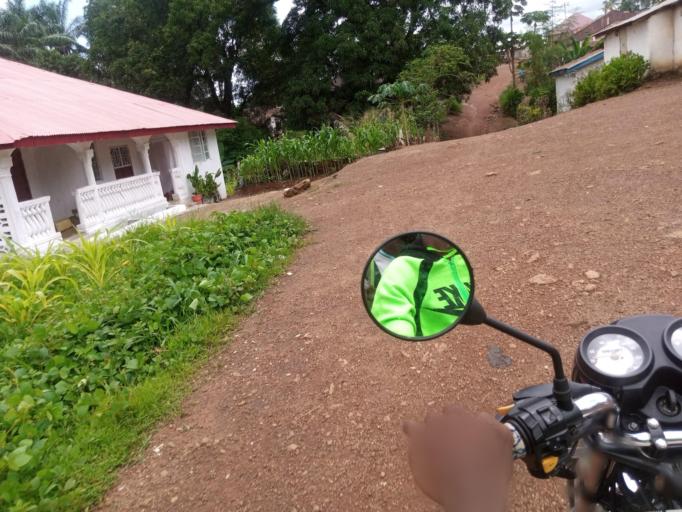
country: SL
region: Northern Province
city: Port Loko
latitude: 8.7629
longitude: -12.7842
